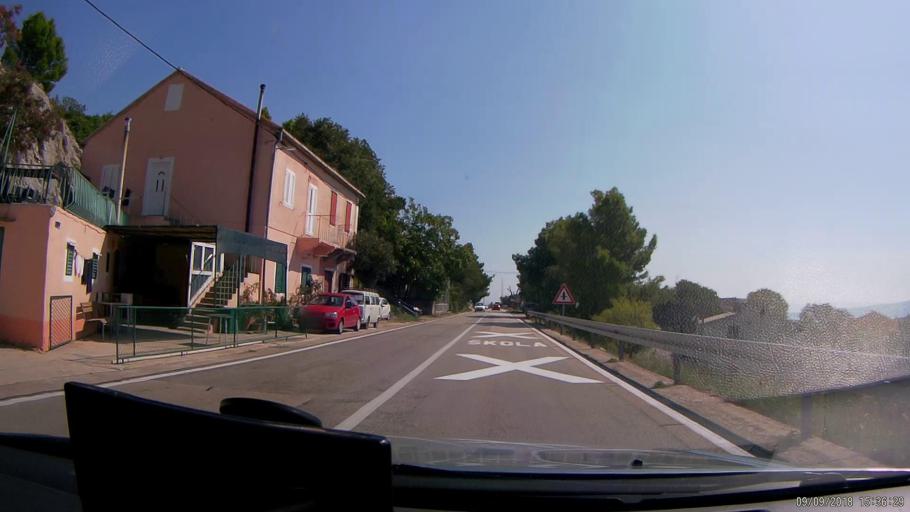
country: HR
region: Splitsko-Dalmatinska
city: Donja Brela
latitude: 43.3779
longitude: 16.9229
